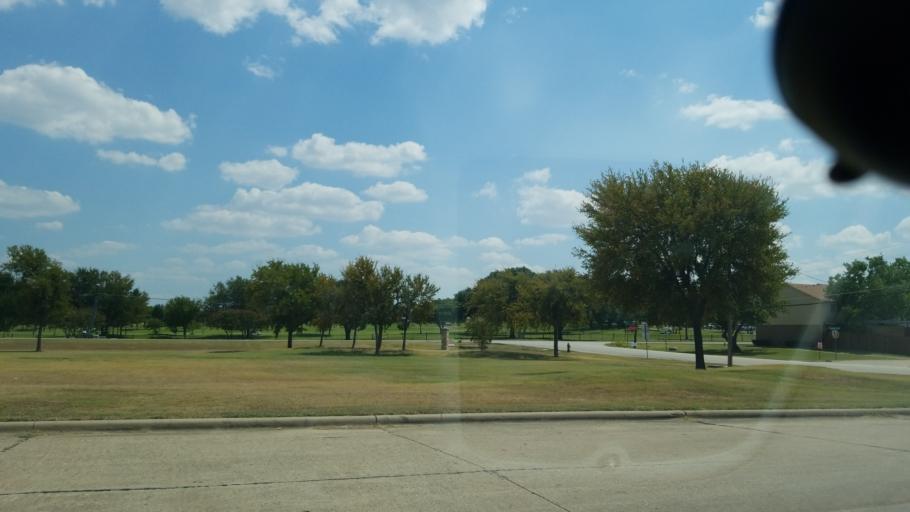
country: US
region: Texas
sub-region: Dallas County
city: Grand Prairie
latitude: 32.6992
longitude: -96.9865
